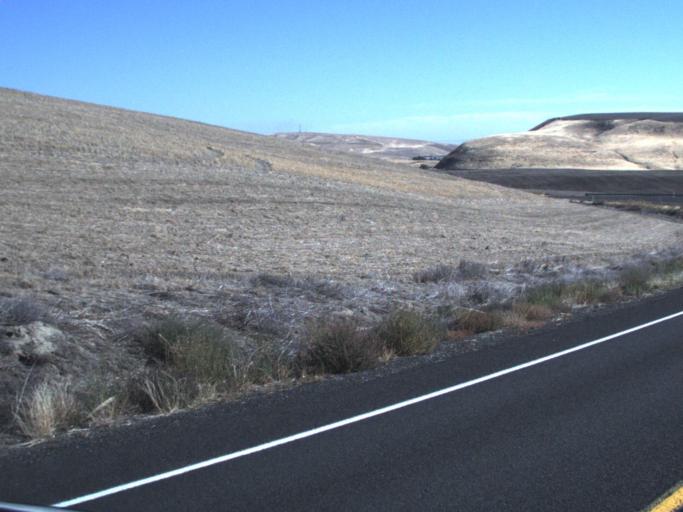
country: US
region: Washington
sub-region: Walla Walla County
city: Garrett
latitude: 46.2888
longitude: -118.5535
